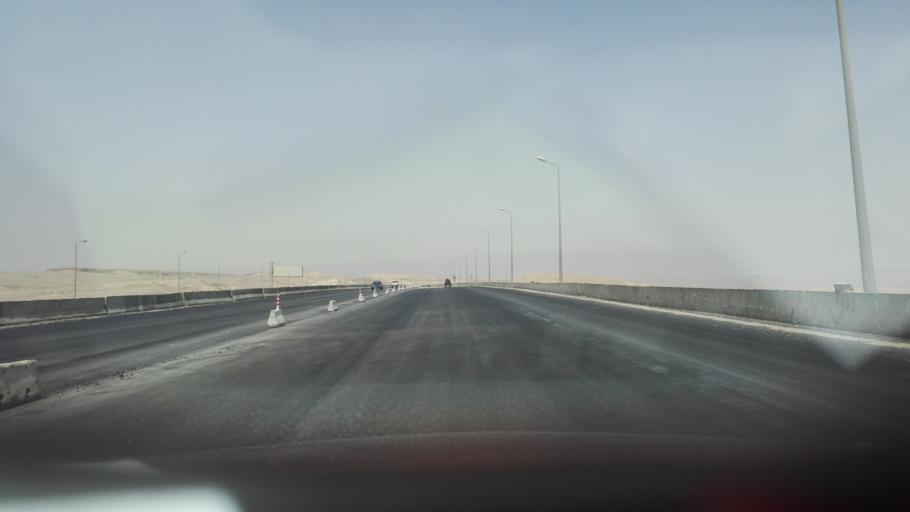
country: EG
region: As Suways
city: Ain Sukhna
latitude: 29.6761
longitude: 32.2281
